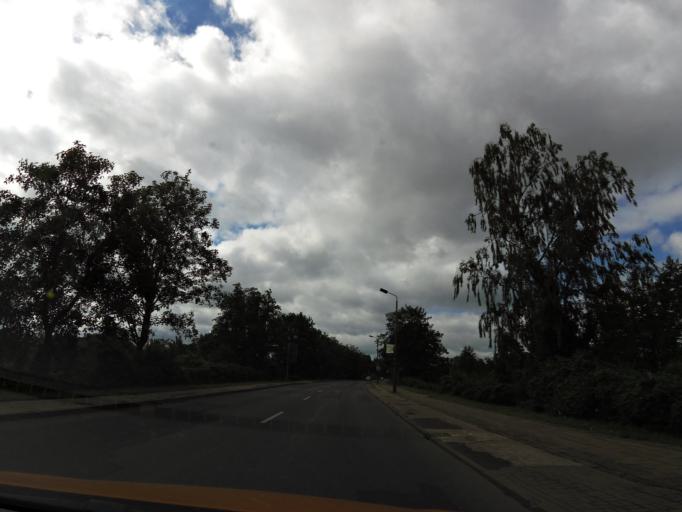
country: DE
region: Mecklenburg-Vorpommern
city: Guestrow
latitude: 53.7922
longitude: 12.1844
